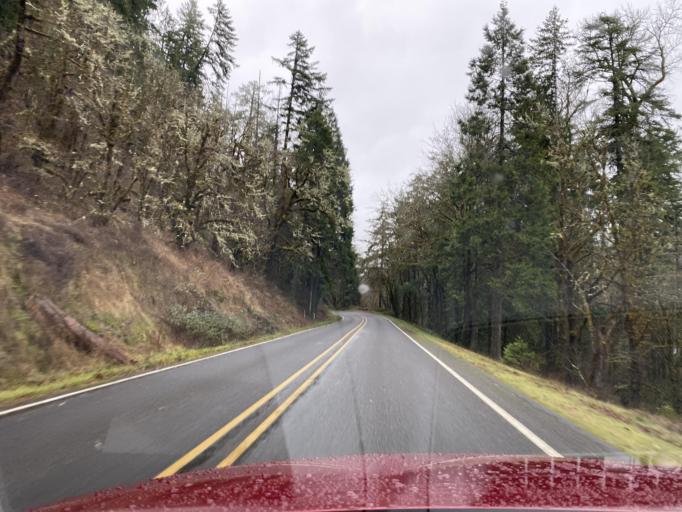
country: US
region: Oregon
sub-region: Lane County
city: Oakridge
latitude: 43.7499
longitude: -122.5252
